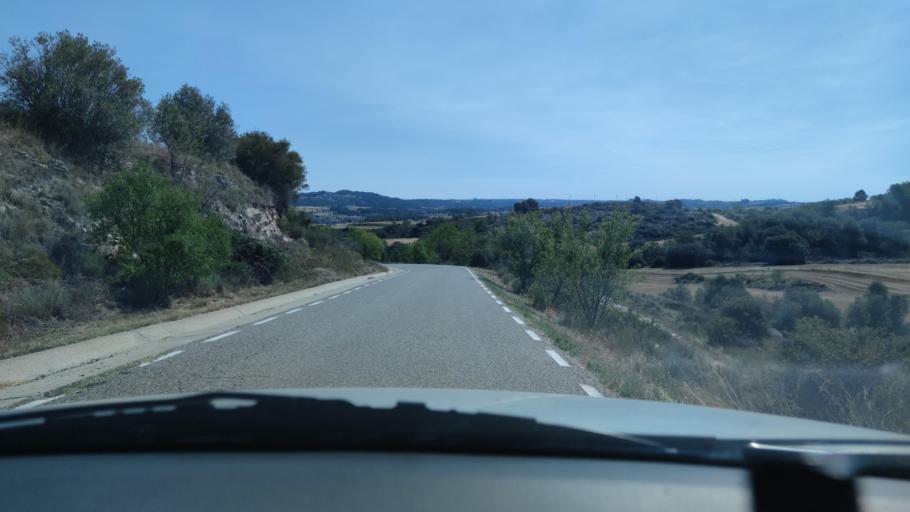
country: ES
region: Catalonia
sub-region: Provincia de Lleida
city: Cervera
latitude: 41.6258
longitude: 1.3231
